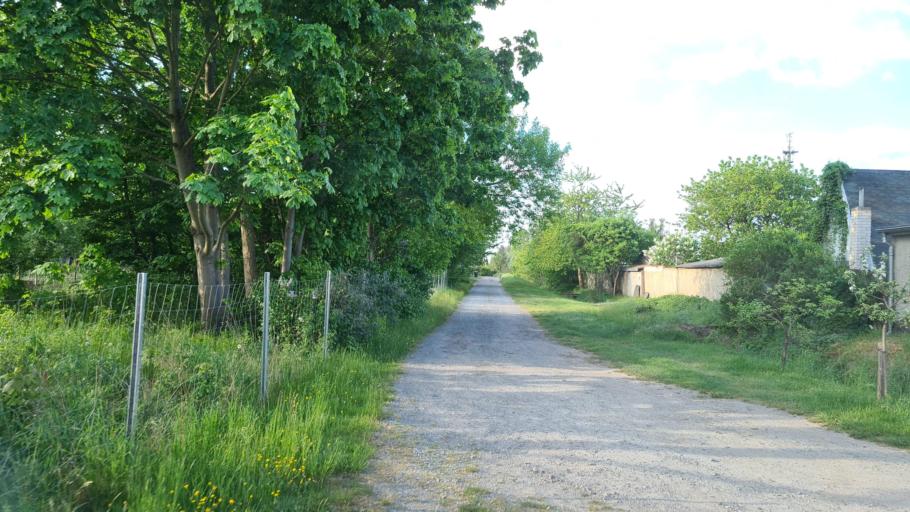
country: DE
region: Brandenburg
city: Falkenberg
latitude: 51.5840
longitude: 13.2277
